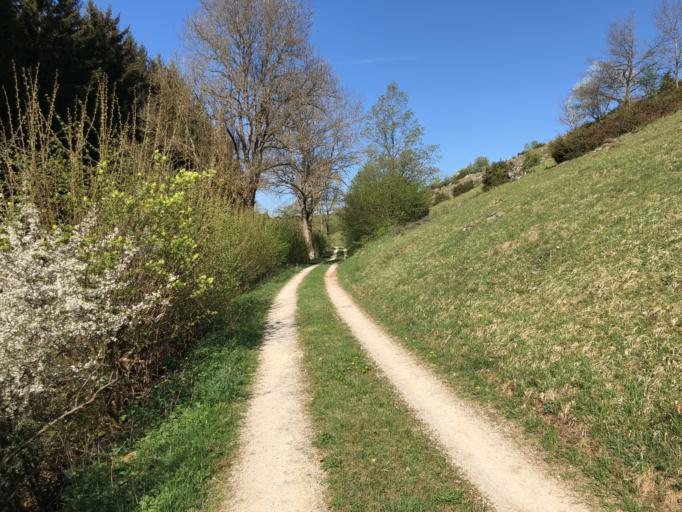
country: DE
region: Baden-Wuerttemberg
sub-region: Tuebingen Region
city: Berghulen
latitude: 48.4810
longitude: 9.7511
